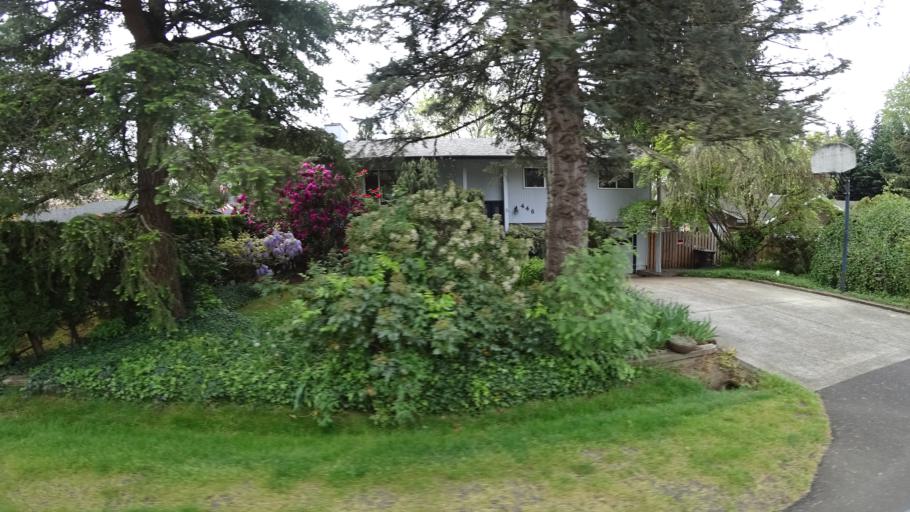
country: US
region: Oregon
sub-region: Washington County
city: Hillsboro
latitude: 45.5270
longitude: -122.9994
